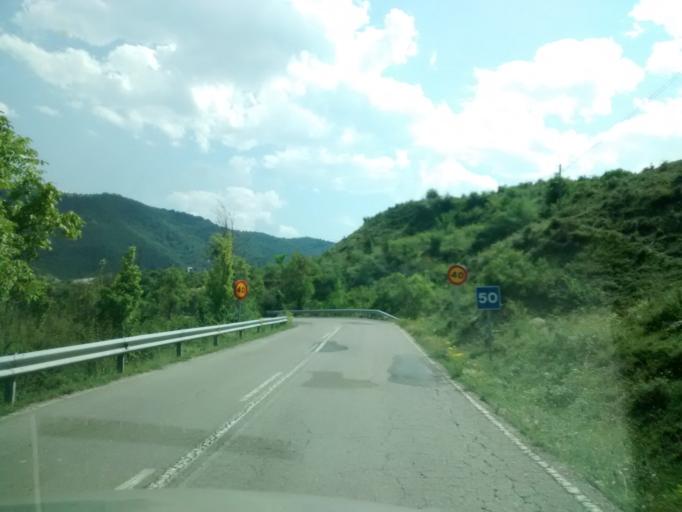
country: ES
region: La Rioja
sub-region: Provincia de La Rioja
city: Soto en Cameros
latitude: 42.2728
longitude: -2.4322
